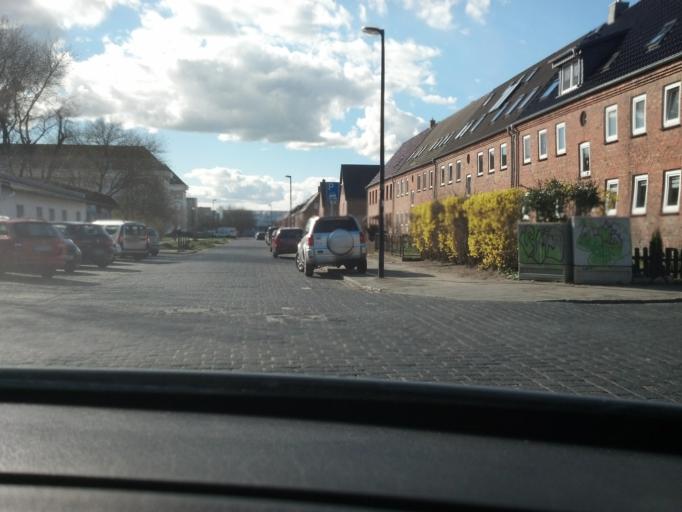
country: DE
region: Mecklenburg-Vorpommern
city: Neubrandenburg
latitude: 53.5637
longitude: 13.2625
